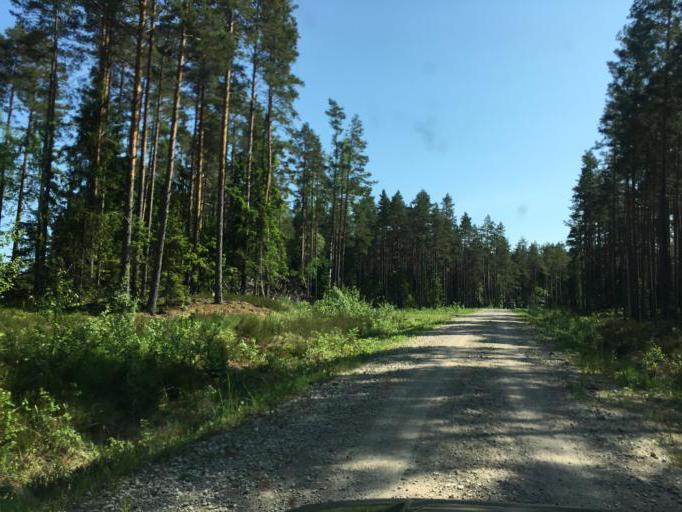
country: LV
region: Dundaga
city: Dundaga
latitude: 57.4495
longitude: 22.3494
